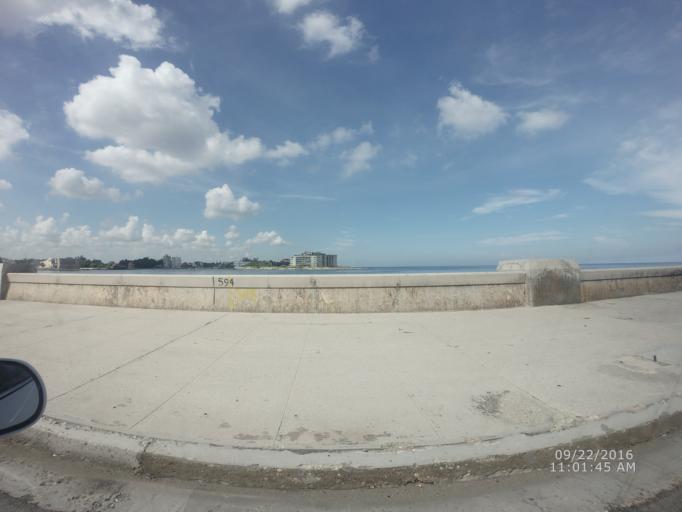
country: CU
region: La Habana
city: Havana
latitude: 23.1354
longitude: -82.4081
